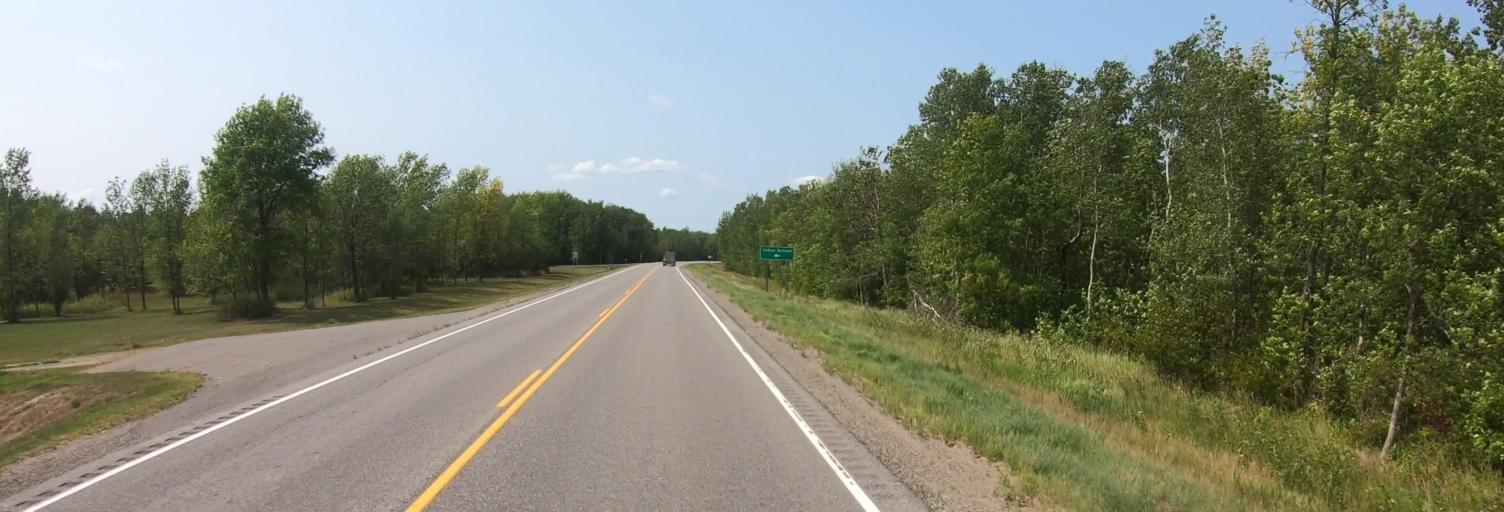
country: US
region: Minnesota
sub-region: Koochiching County
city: International Falls
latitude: 48.6307
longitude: -93.8947
